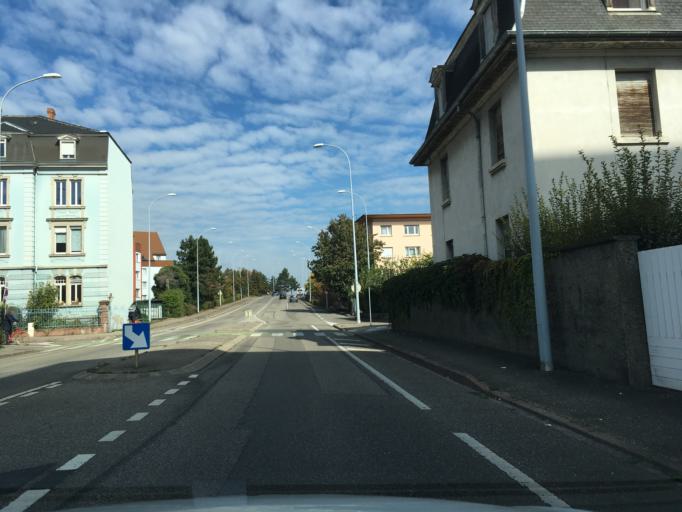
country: FR
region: Alsace
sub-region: Departement du Haut-Rhin
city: Colmar
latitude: 48.0770
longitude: 7.3478
